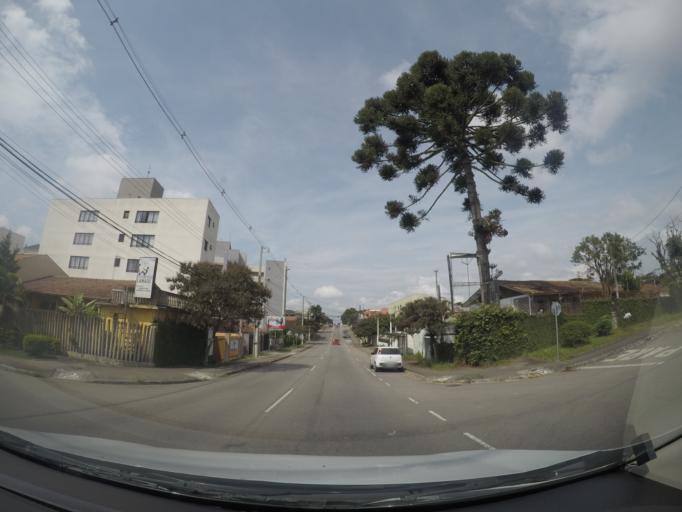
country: BR
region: Parana
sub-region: Curitiba
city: Curitiba
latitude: -25.4899
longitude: -49.2893
